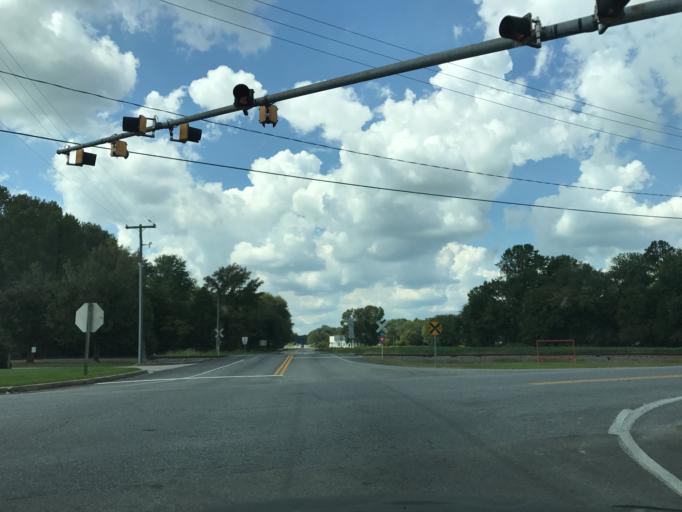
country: US
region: Maryland
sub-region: Caroline County
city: Greensboro
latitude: 39.1446
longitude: -75.8643
